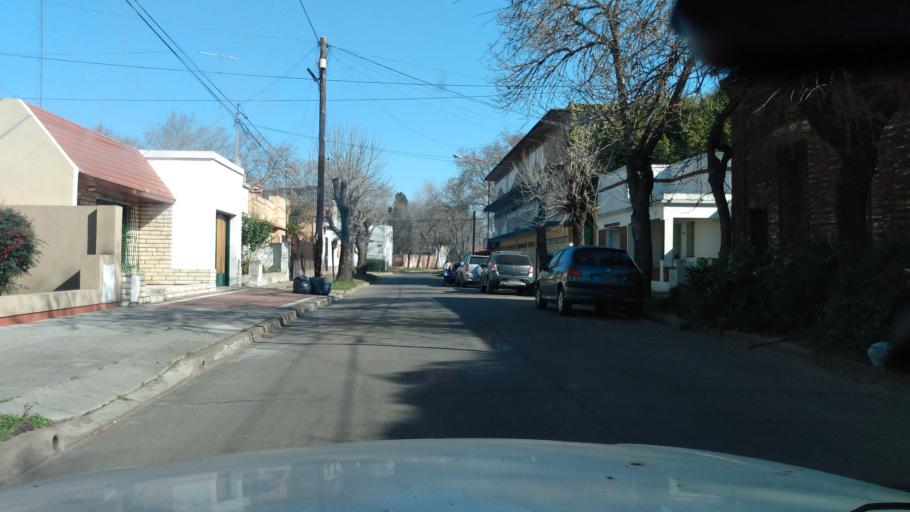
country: AR
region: Buenos Aires
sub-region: Partido de Lujan
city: Lujan
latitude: -34.5734
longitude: -59.1093
